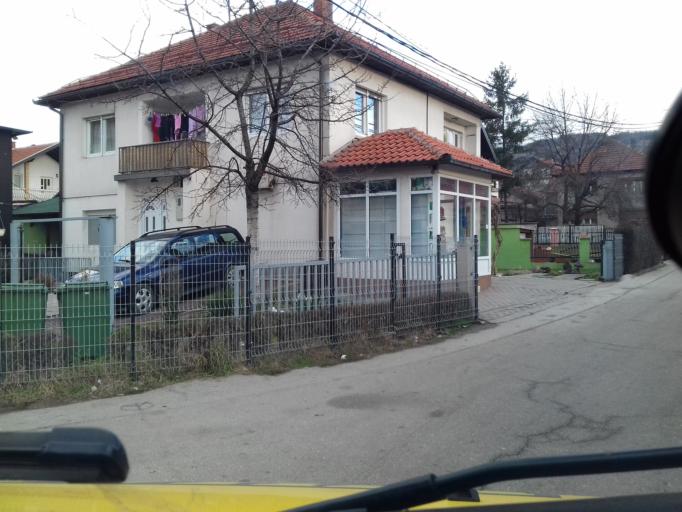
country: BA
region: Federation of Bosnia and Herzegovina
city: Zenica
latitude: 44.2171
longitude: 17.9159
